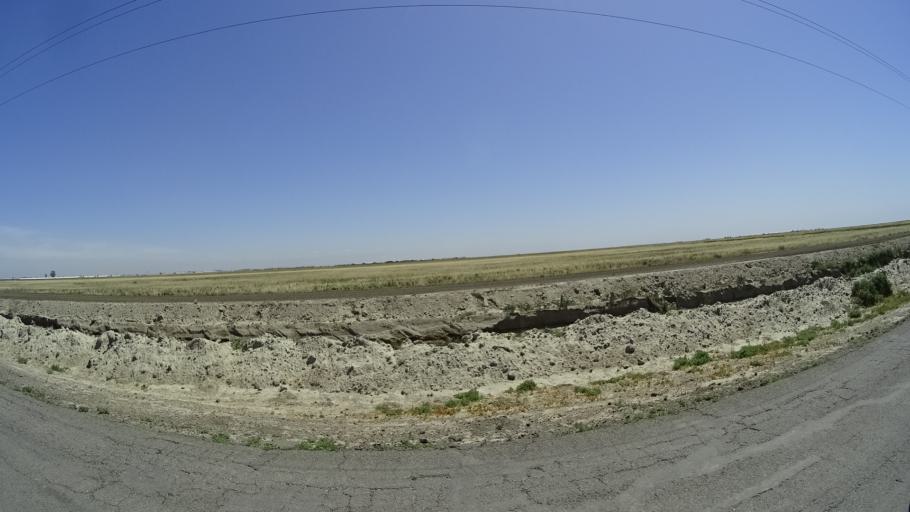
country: US
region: California
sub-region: Kings County
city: Stratford
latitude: 36.1836
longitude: -119.7175
